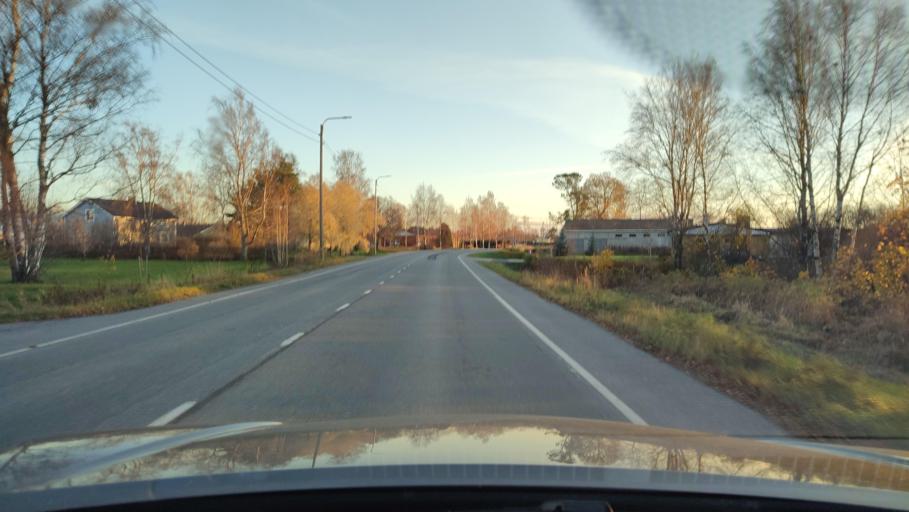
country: FI
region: Ostrobothnia
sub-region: Sydosterbotten
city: Naerpes
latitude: 62.4629
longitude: 21.3560
